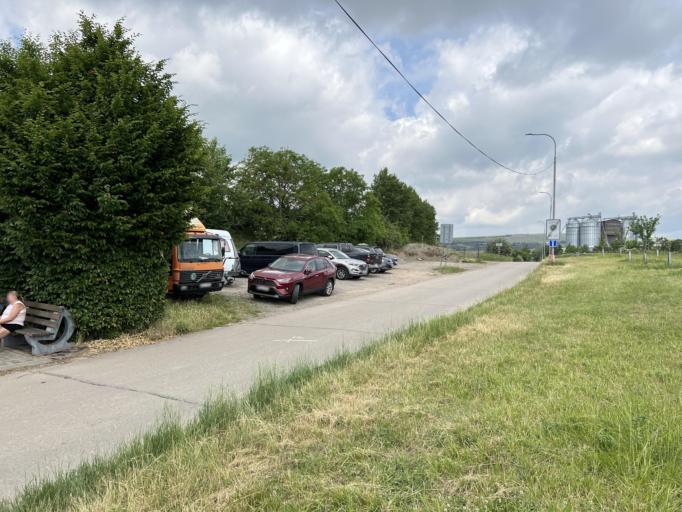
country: CZ
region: South Moravian
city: Sardice
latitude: 48.9739
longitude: 17.0274
